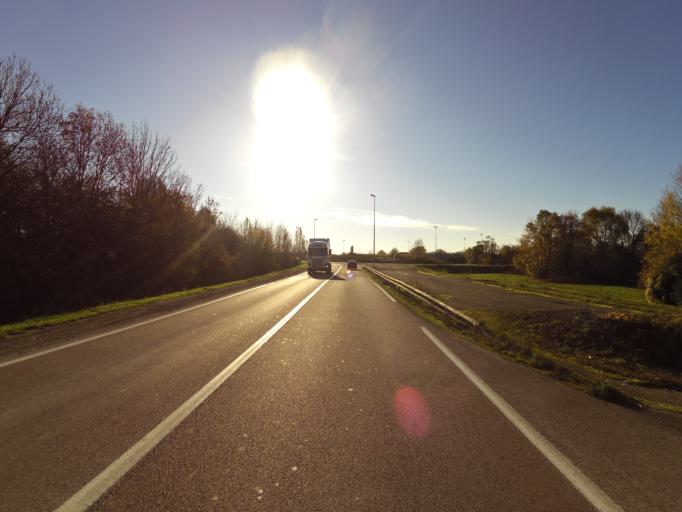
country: FR
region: Champagne-Ardenne
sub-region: Departement de l'Aube
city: Bucheres
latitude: 48.2278
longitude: 4.1305
